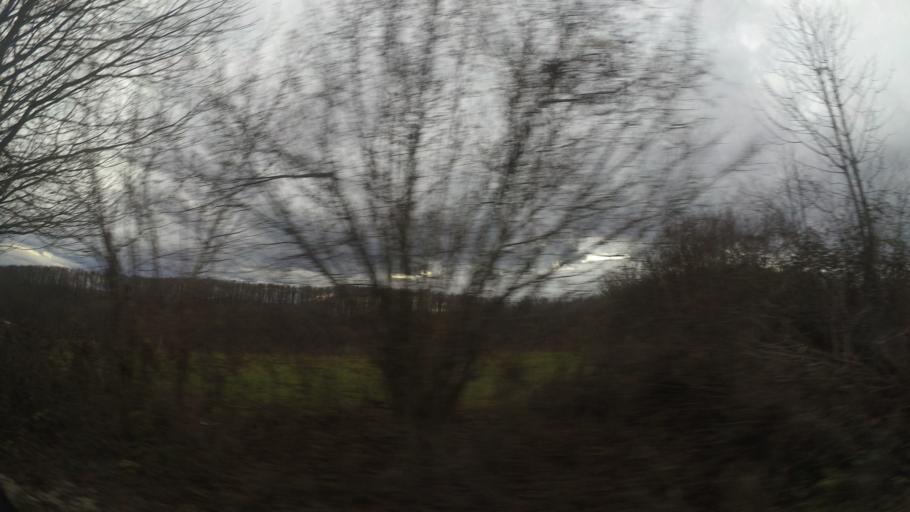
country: HR
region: Karlovacka
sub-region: Grad Karlovac
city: Karlovac
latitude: 45.3854
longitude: 15.5407
